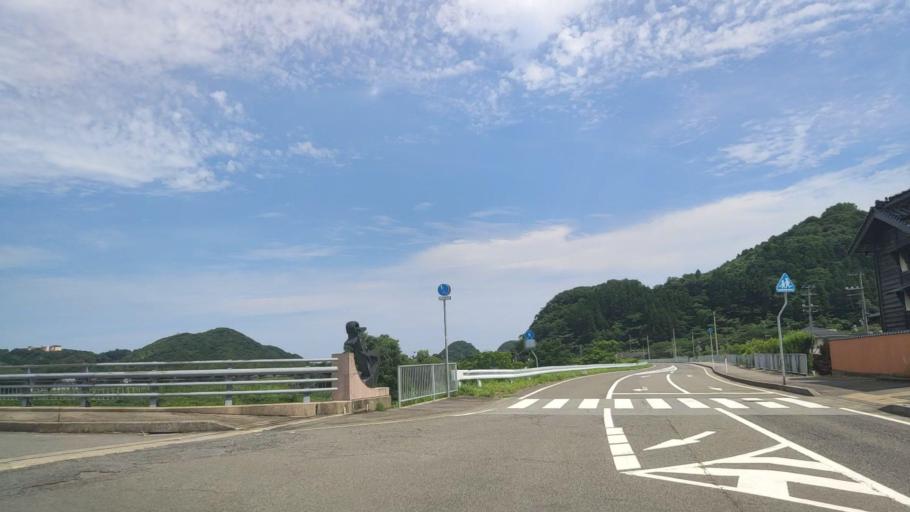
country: JP
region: Hyogo
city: Toyooka
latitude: 35.6483
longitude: 134.7636
